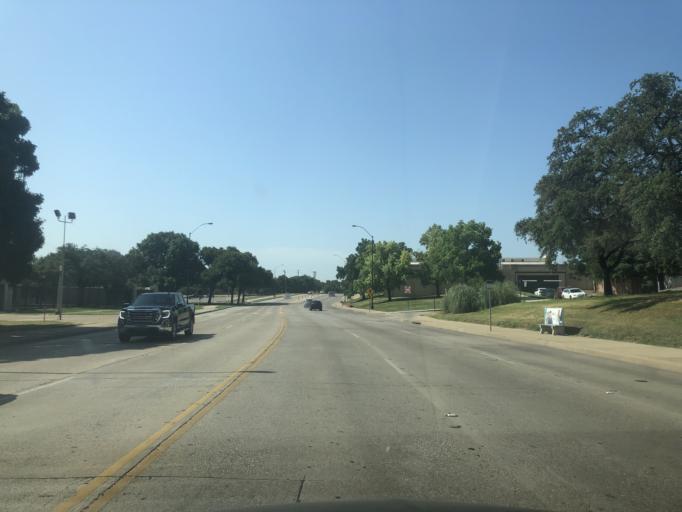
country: US
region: Texas
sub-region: Tarrant County
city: River Oaks
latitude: 32.7463
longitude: -97.3619
